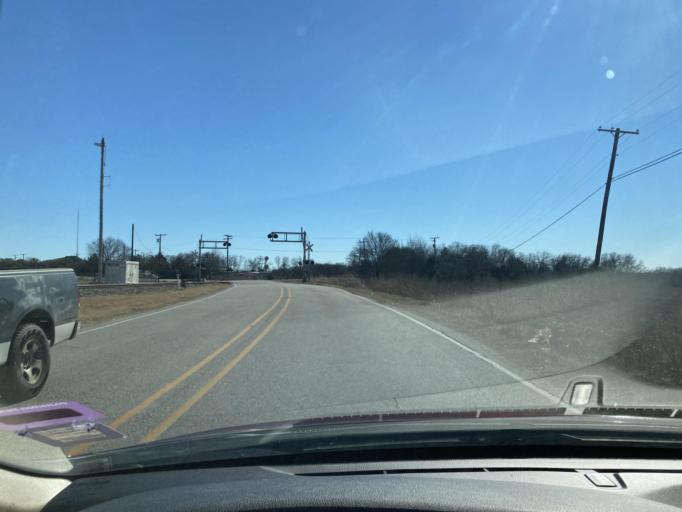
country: US
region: Texas
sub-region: Navarro County
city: Corsicana
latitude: 32.0688
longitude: -96.4637
